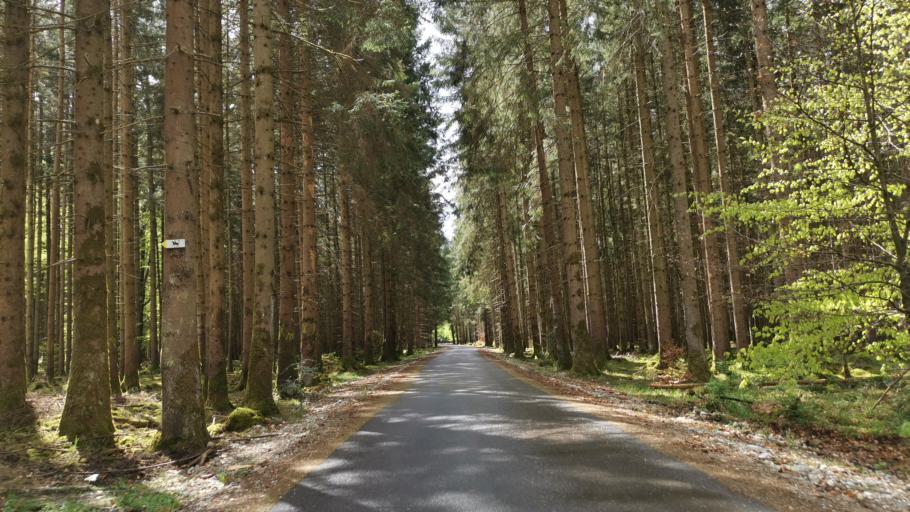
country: DE
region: Bavaria
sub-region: Upper Bavaria
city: Pullach im Isartal
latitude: 48.0622
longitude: 11.4894
